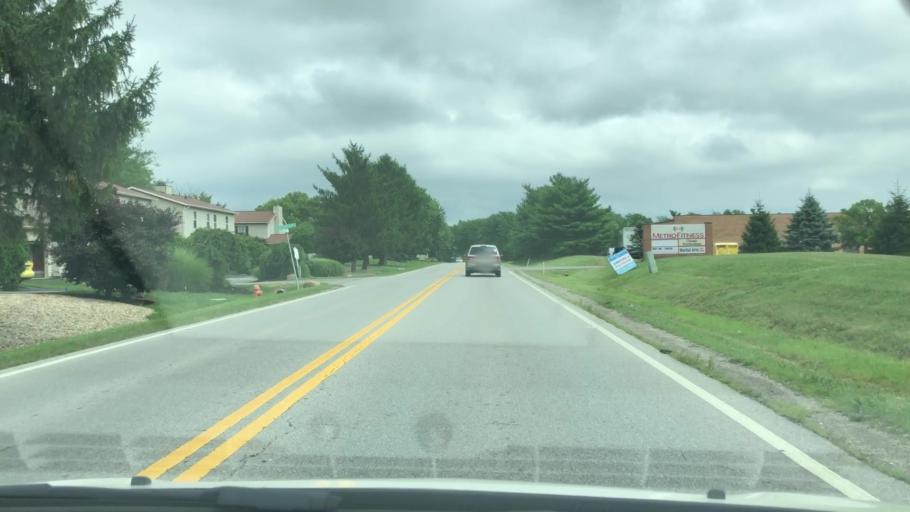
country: US
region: Ohio
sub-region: Franklin County
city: Worthington
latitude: 40.1180
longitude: -82.9852
